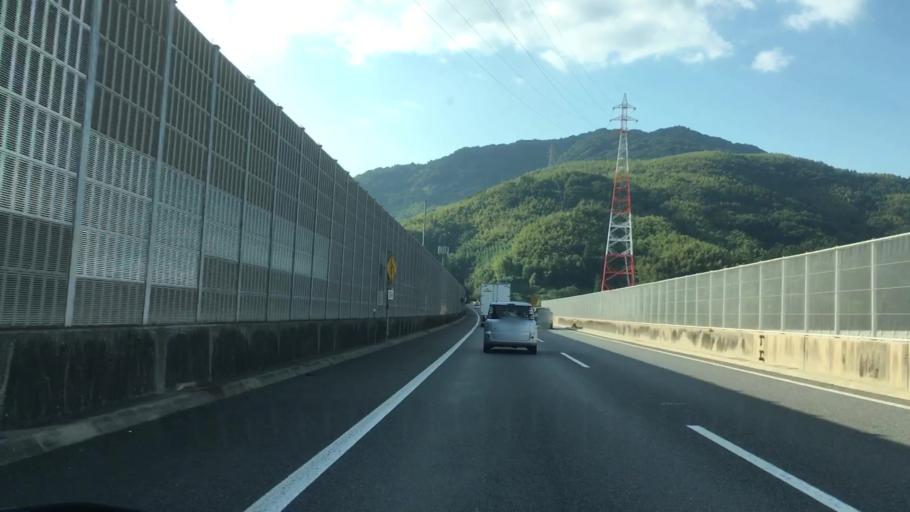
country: JP
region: Yamaguchi
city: Tokuyama
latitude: 34.0862
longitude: 131.7813
